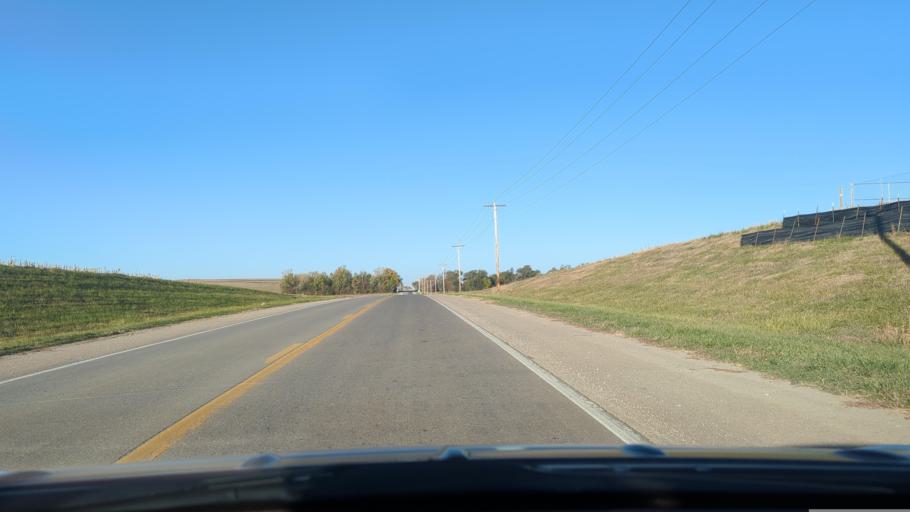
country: US
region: Nebraska
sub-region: Sarpy County
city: Springfield
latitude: 41.1036
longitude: -96.1499
